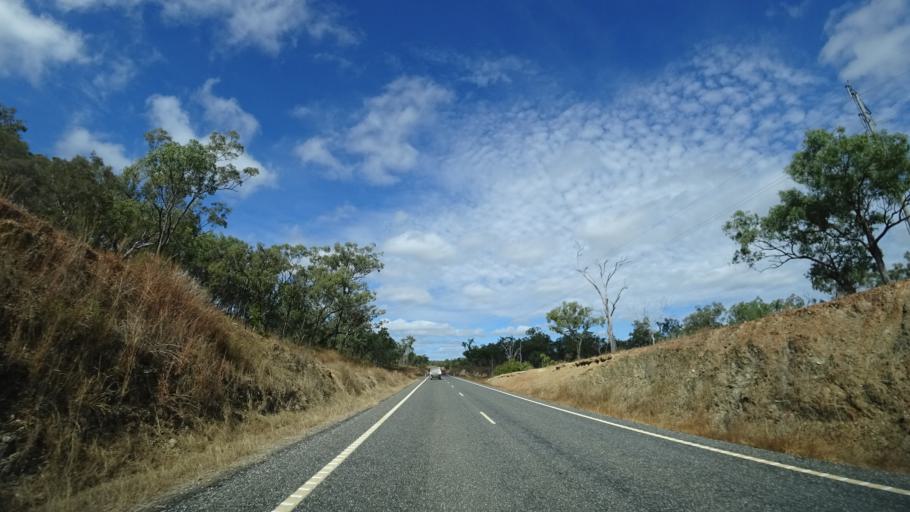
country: AU
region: Queensland
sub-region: Cairns
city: Port Douglas
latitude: -16.2928
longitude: 144.7159
